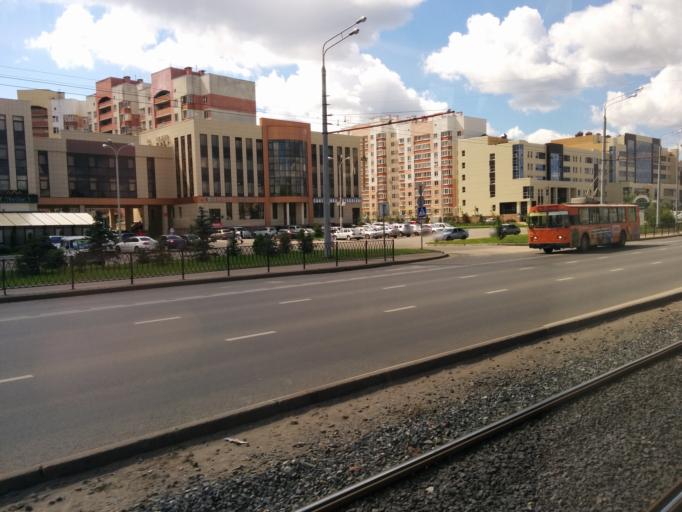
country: RU
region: Tatarstan
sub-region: Gorod Kazan'
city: Kazan
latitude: 55.8272
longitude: 49.1120
